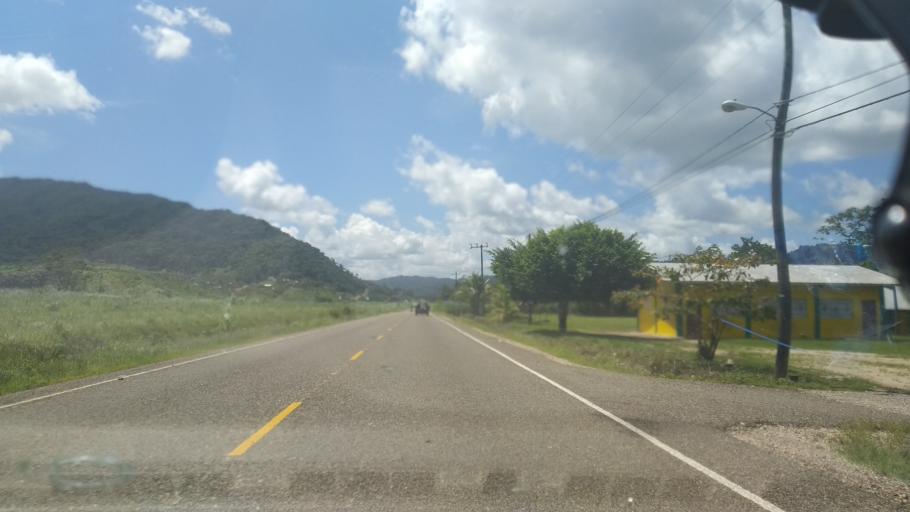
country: BZ
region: Stann Creek
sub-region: Dangriga
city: Dangriga
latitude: 17.0271
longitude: -88.5124
